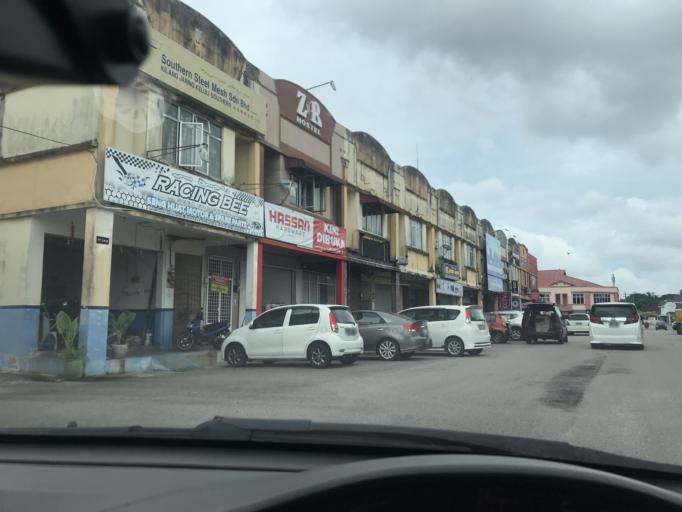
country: MY
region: Kelantan
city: Kota Bharu
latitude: 6.1201
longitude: 102.2167
